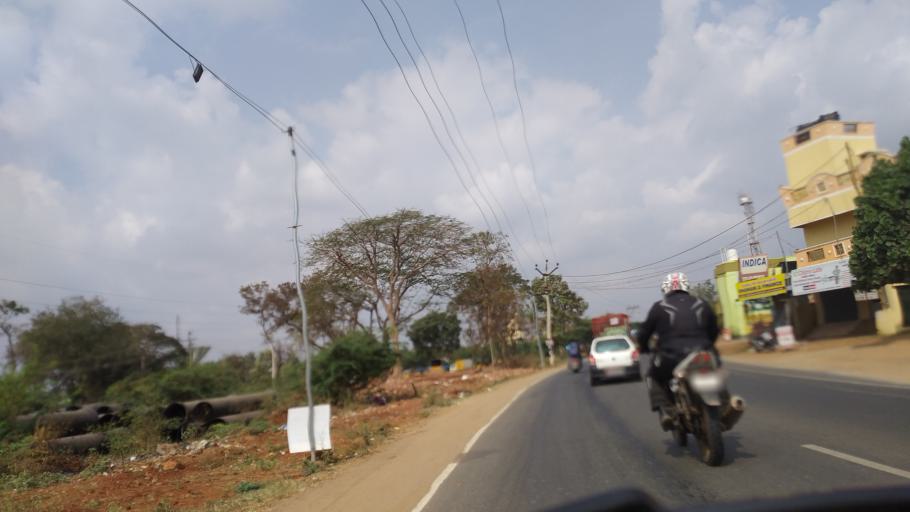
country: IN
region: Tamil Nadu
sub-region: Coimbatore
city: Perur
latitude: 10.9448
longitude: 76.9387
